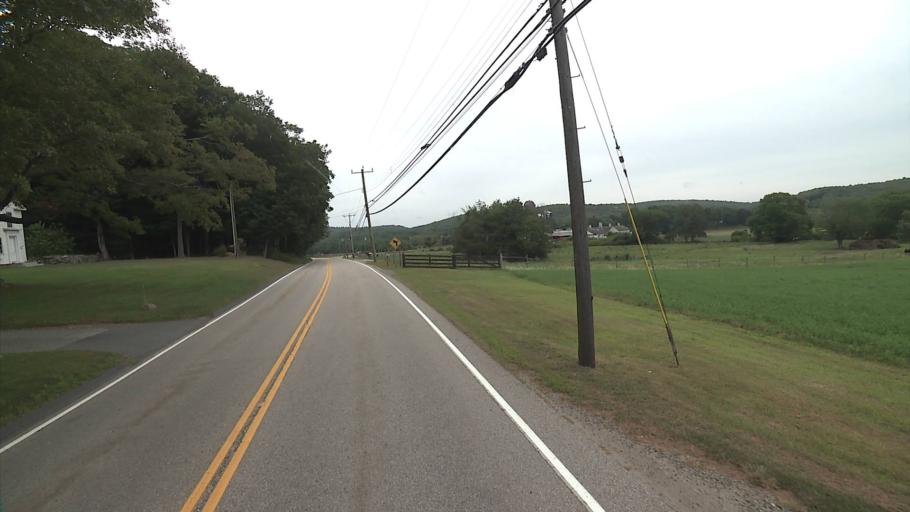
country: US
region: Connecticut
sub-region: Middlesex County
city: Essex Village
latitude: 41.3745
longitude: -72.3473
